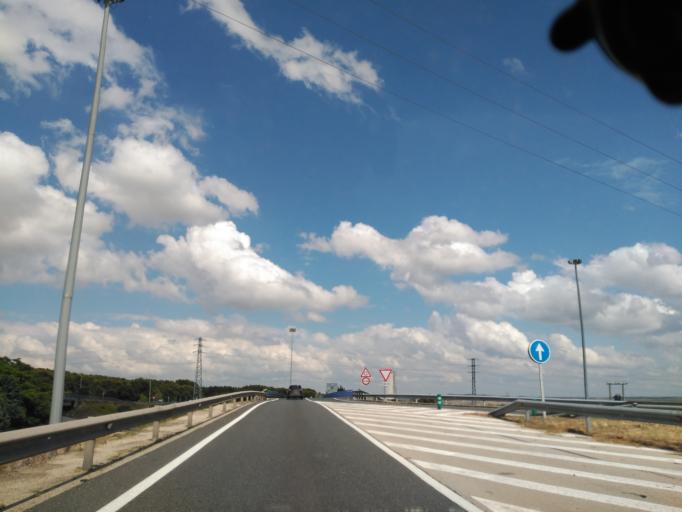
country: ES
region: Madrid
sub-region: Provincia de Madrid
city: Getafe
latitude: 40.3035
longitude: -3.6930
